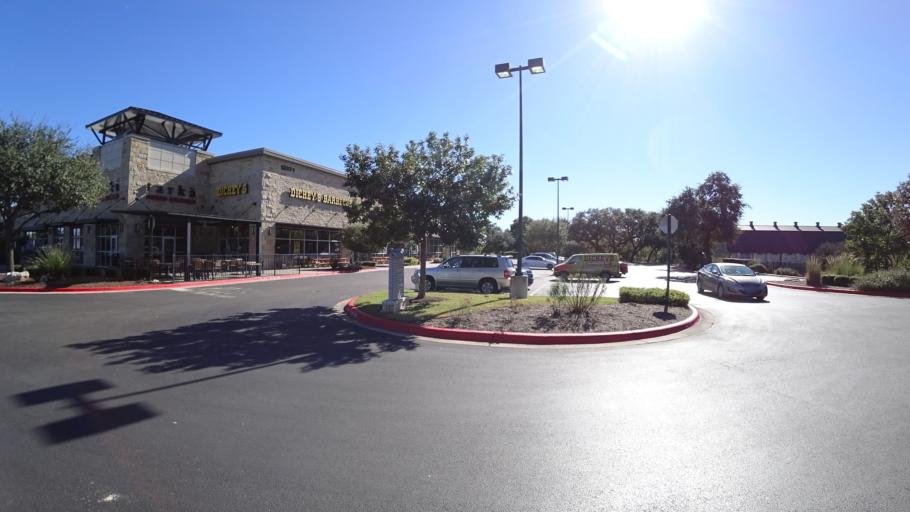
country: US
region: Texas
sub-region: Travis County
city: Rollingwood
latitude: 30.2312
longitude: -97.8177
